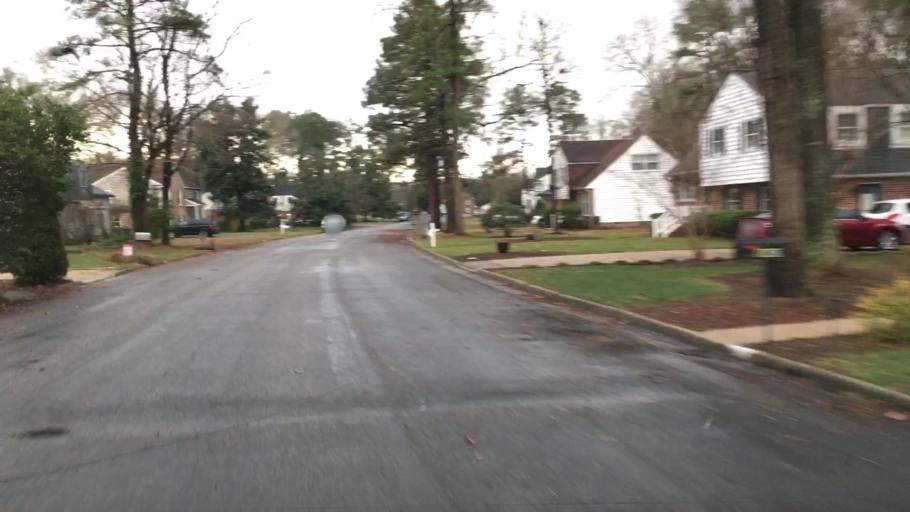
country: US
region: Virginia
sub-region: Chesterfield County
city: Bon Air
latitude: 37.5151
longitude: -77.6202
